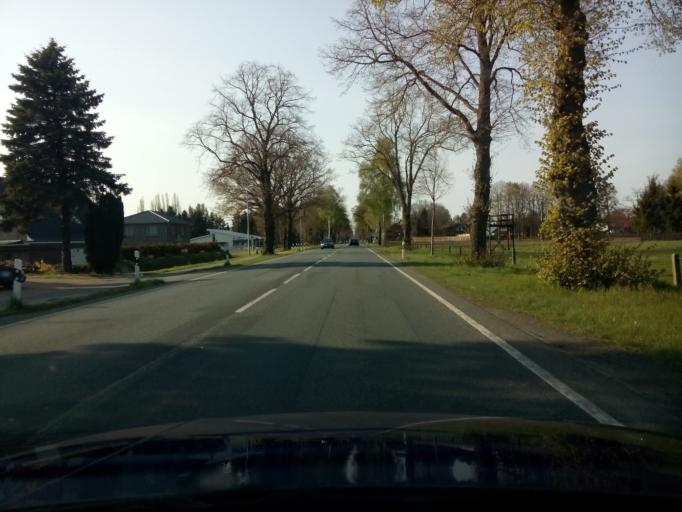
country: DE
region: Lower Saxony
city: Syke
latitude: 52.9681
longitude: 8.7960
